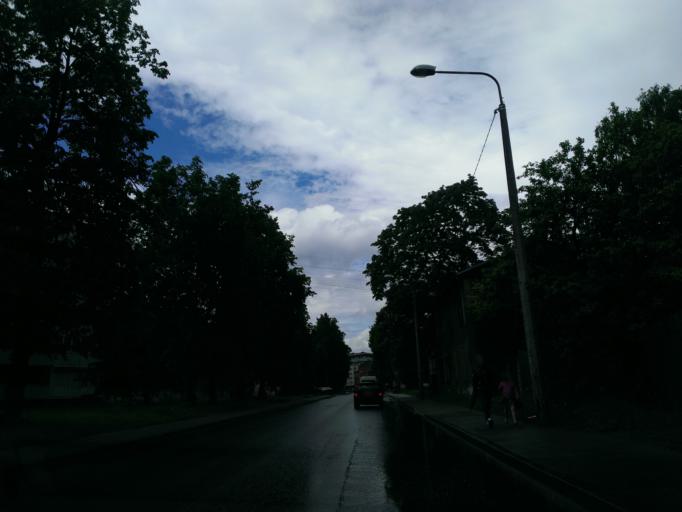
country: LV
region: Riga
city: Riga
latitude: 56.9235
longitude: 24.0946
